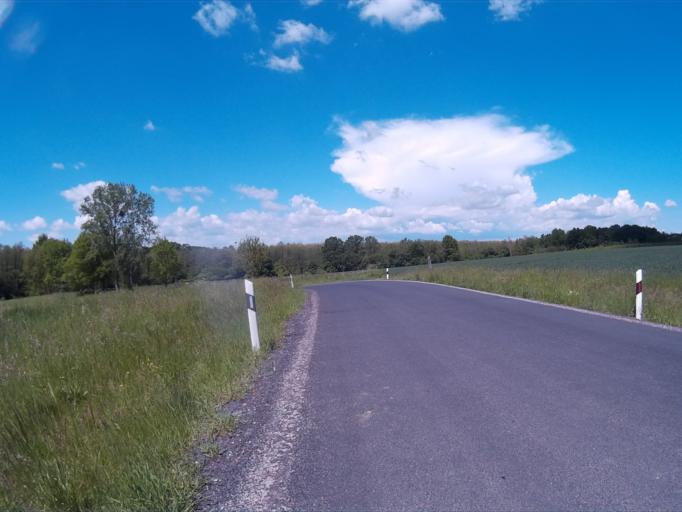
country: HU
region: Vas
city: Kormend
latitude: 46.9671
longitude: 16.5757
